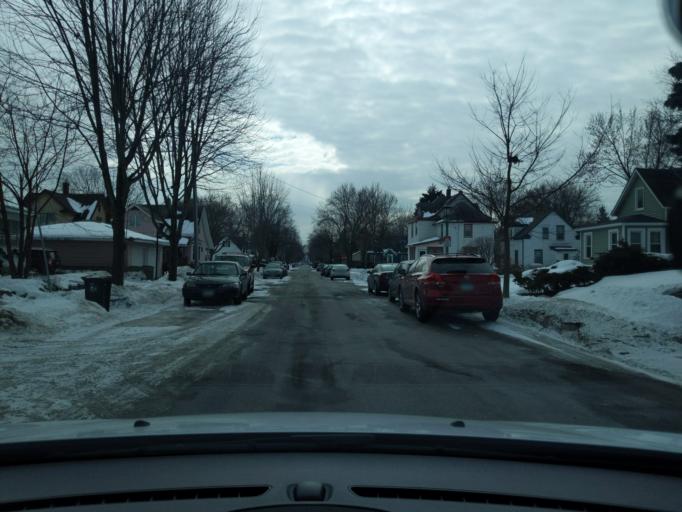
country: US
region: Minnesota
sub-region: Ramsey County
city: Falcon Heights
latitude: 44.9674
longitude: -93.1607
